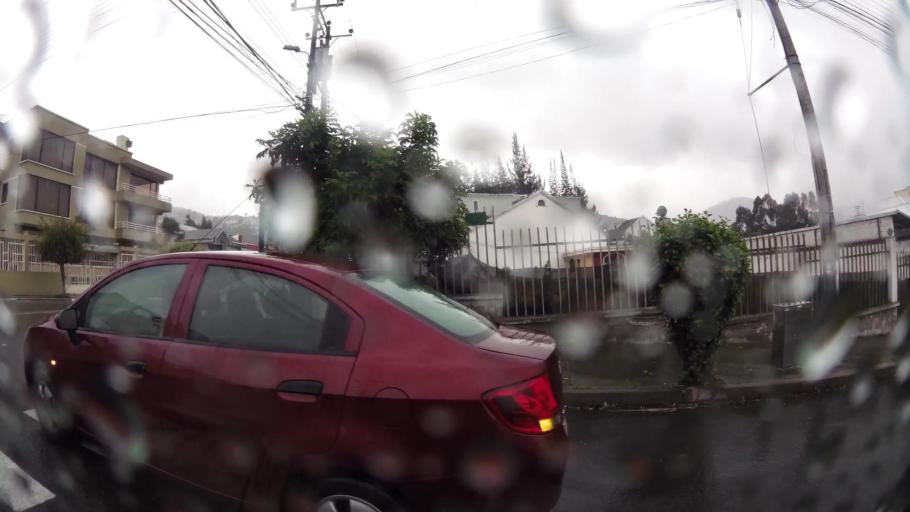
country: EC
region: Pichincha
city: Quito
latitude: -0.1019
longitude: -78.5027
